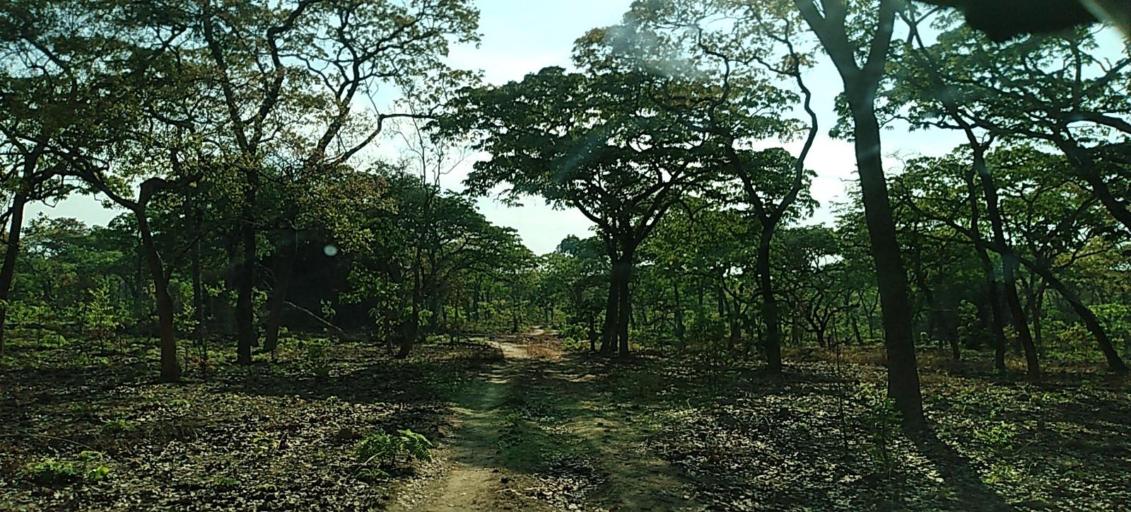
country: ZM
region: North-Western
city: Kalengwa
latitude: -13.2356
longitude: 25.0596
